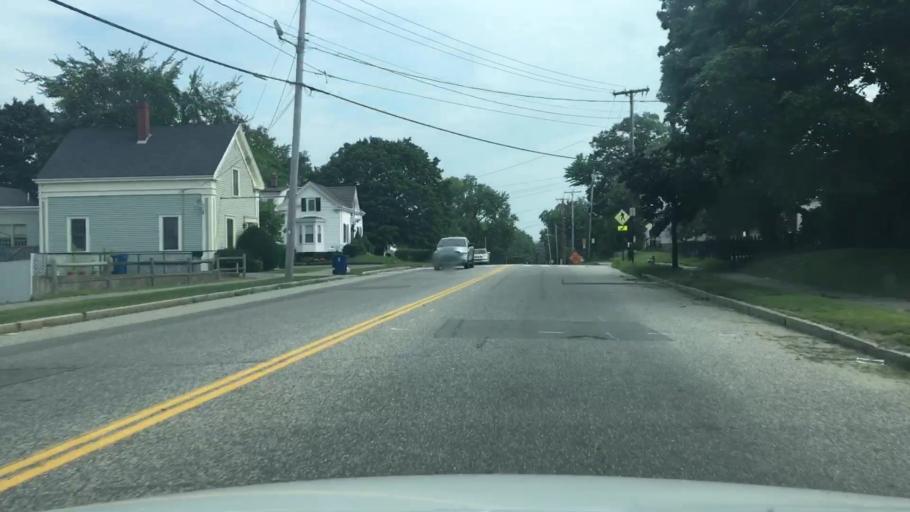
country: US
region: Maine
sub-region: Cumberland County
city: Portland
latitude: 43.6905
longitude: -70.2932
